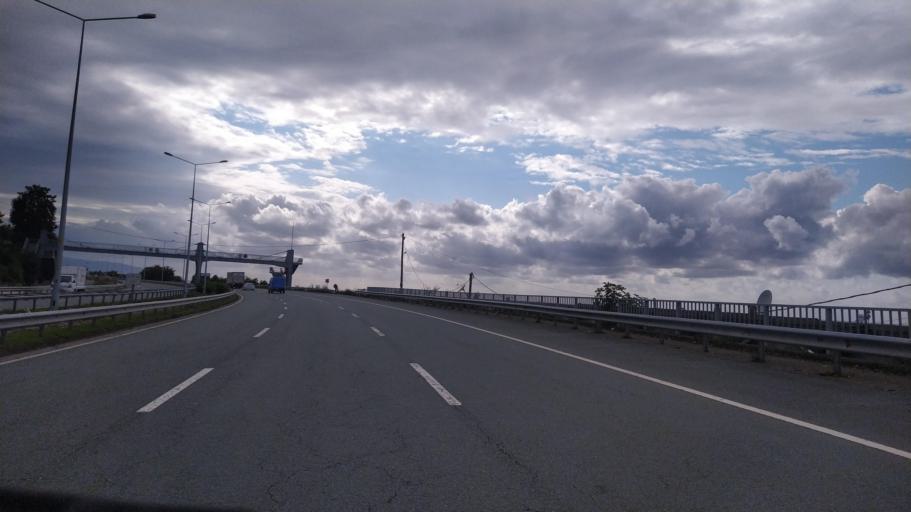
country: TR
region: Rize
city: Ardesen
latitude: 41.2101
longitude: 41.0374
